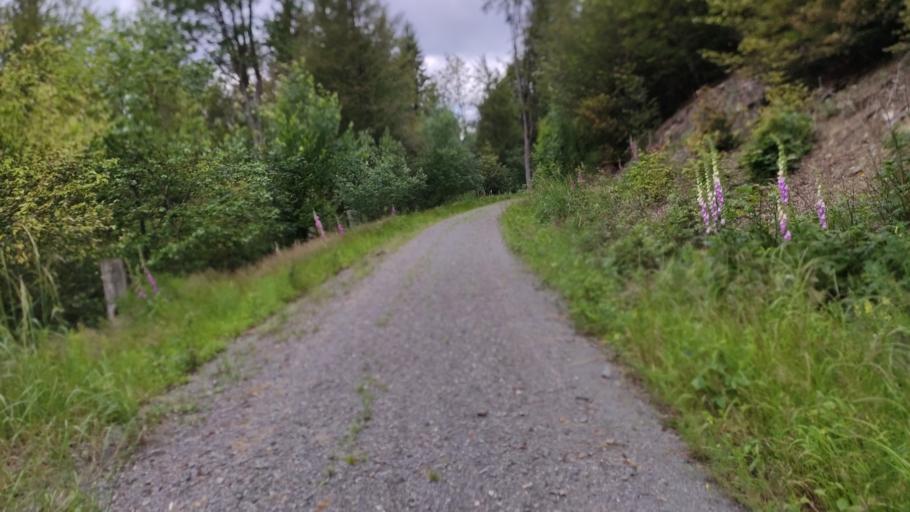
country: DE
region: Bavaria
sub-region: Upper Franconia
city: Nordhalben
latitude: 50.3708
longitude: 11.4763
